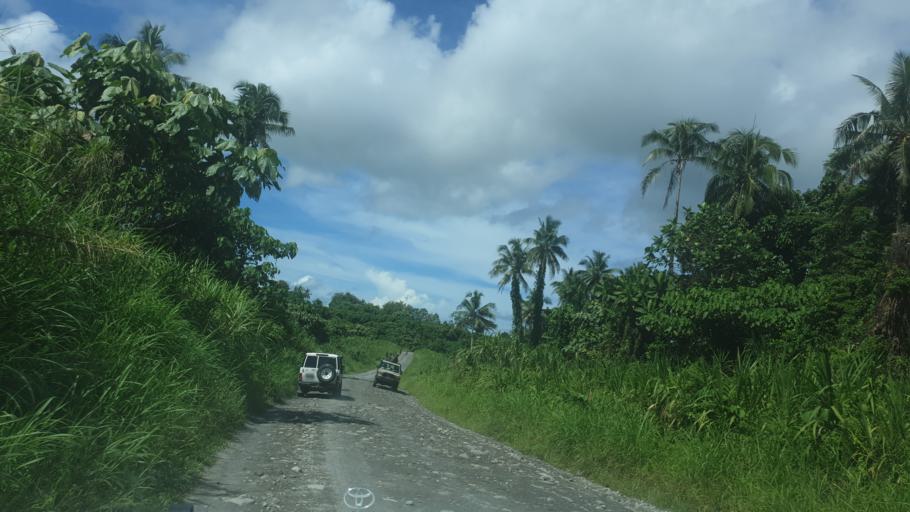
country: PG
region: Bougainville
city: Panguna
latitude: -6.5616
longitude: 155.3559
